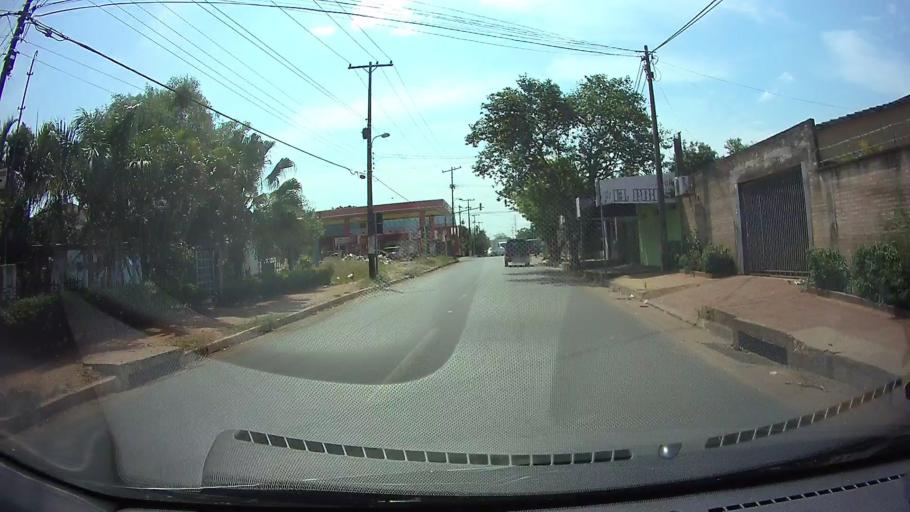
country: PY
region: Central
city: San Lorenzo
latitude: -25.3260
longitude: -57.5010
